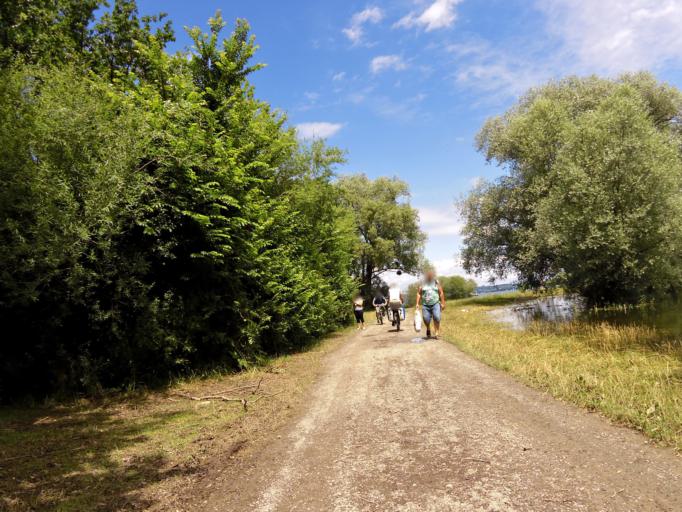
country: AT
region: Vorarlberg
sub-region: Politischer Bezirk Bregenz
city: Hard
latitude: 47.4972
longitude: 9.6785
